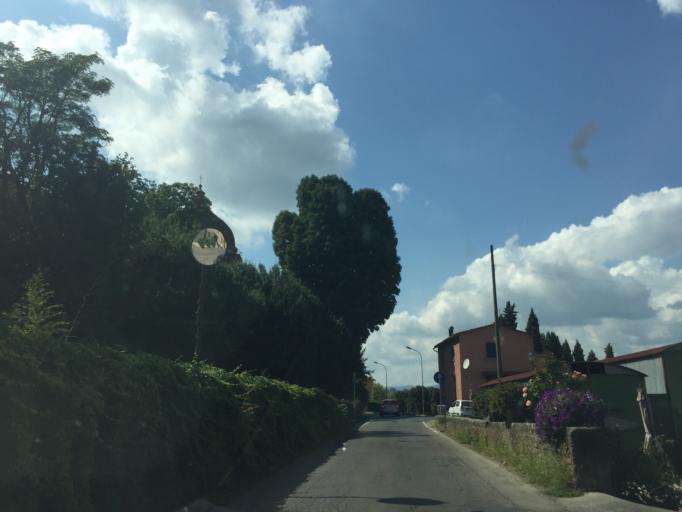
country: IT
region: Tuscany
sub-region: Provincia di Pistoia
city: Cantagrillo-Casalguidi
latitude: 43.8759
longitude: 10.9145
